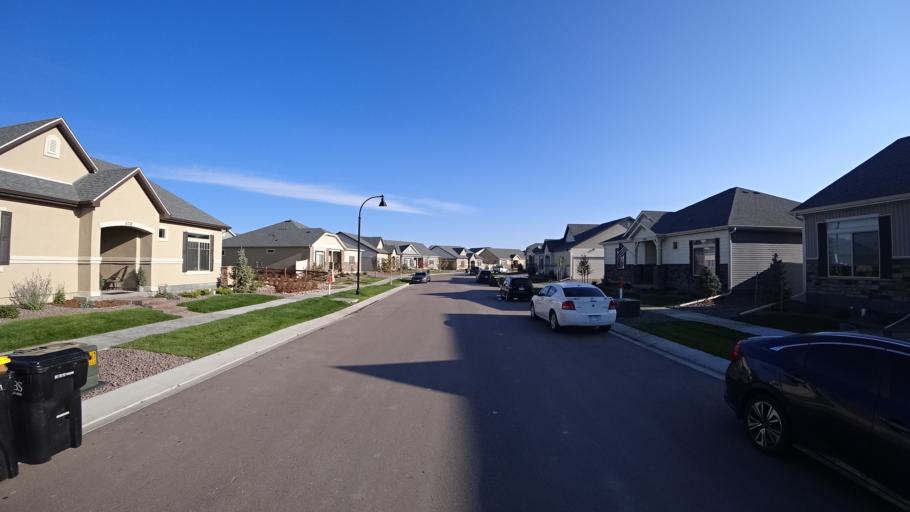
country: US
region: Colorado
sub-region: El Paso County
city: Cimarron Hills
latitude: 38.9276
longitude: -104.6587
